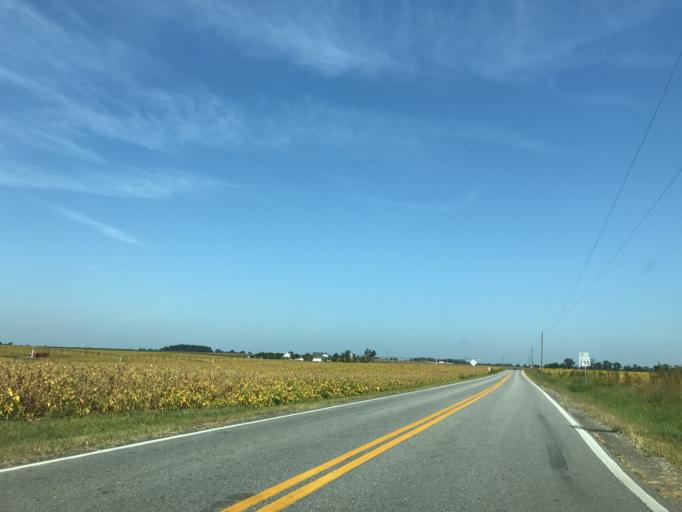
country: US
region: Maryland
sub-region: Queen Anne's County
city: Kingstown
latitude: 39.2740
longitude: -75.9513
